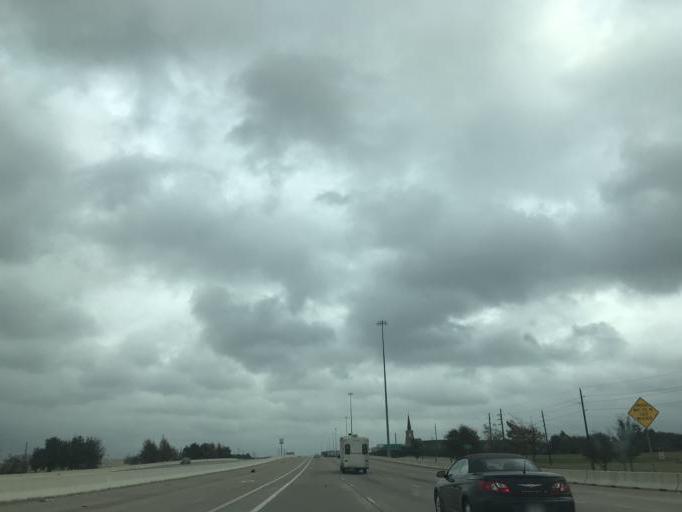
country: US
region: Texas
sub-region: Fort Bend County
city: Sugar Land
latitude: 29.5842
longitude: -95.6428
